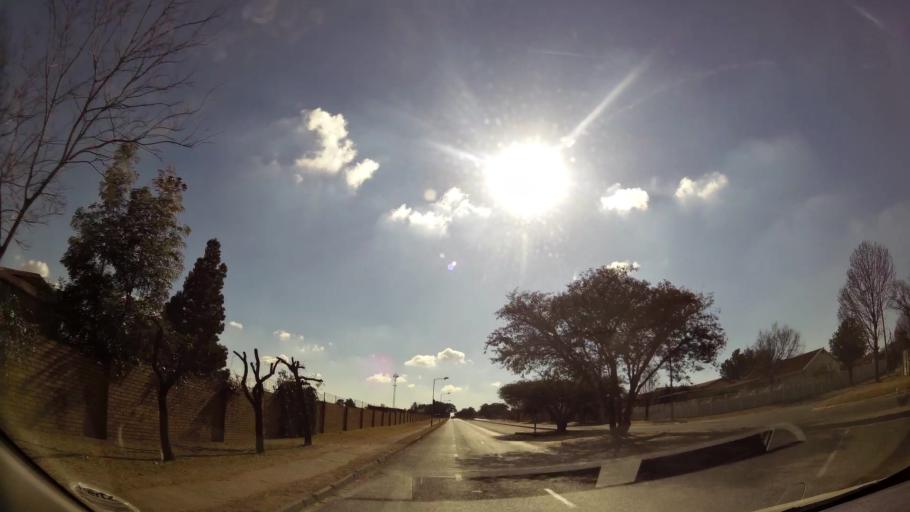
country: ZA
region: Gauteng
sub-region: City of Johannesburg Metropolitan Municipality
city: Roodepoort
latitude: -26.1487
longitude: 27.8229
